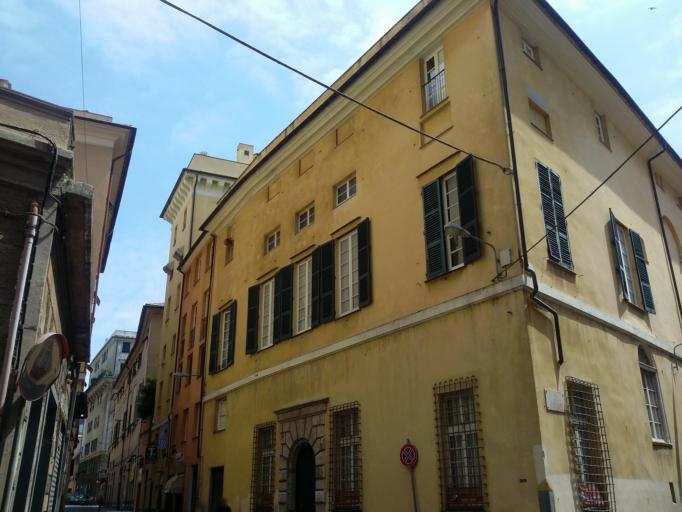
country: IT
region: Liguria
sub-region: Provincia di Genova
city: San Teodoro
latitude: 44.4121
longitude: 8.8909
